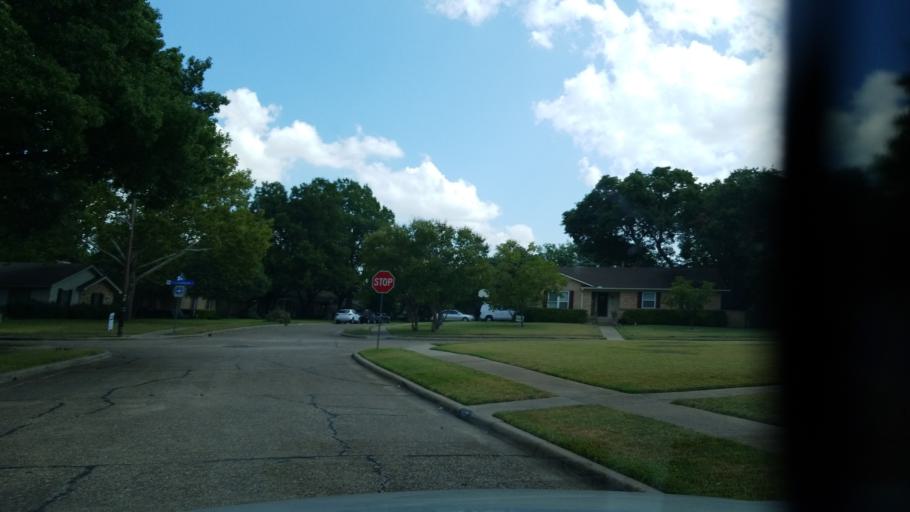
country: US
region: Texas
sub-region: Dallas County
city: Richardson
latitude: 32.9643
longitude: -96.7672
